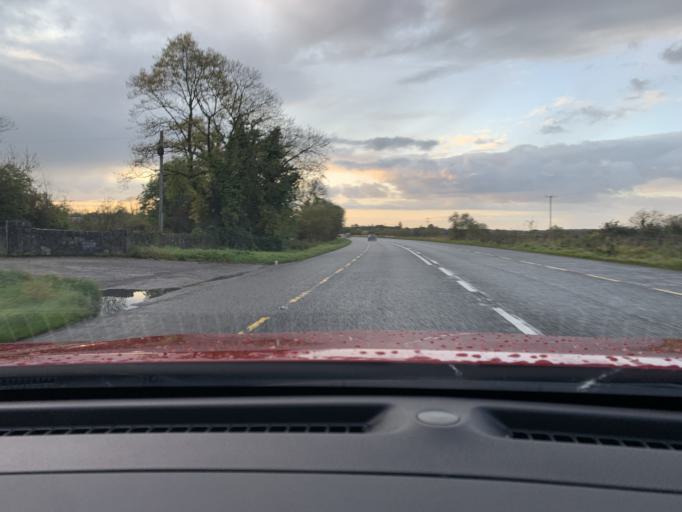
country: IE
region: Connaught
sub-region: County Leitrim
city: Carrick-on-Shannon
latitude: 53.9477
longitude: -8.1235
